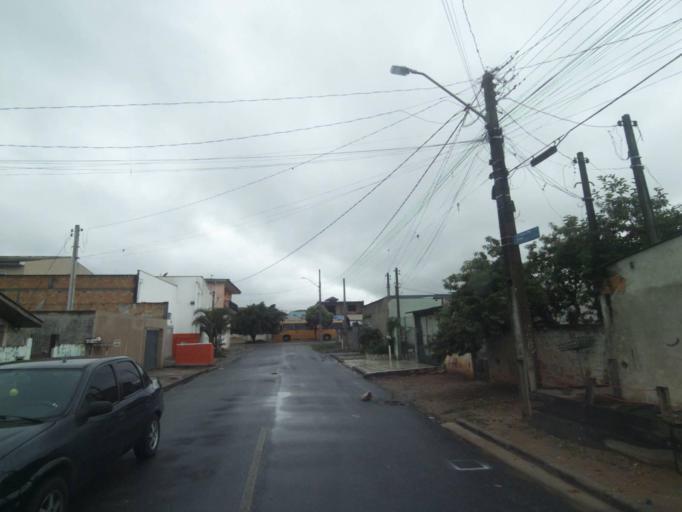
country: BR
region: Parana
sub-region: Araucaria
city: Araucaria
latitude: -25.5325
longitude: -49.3396
